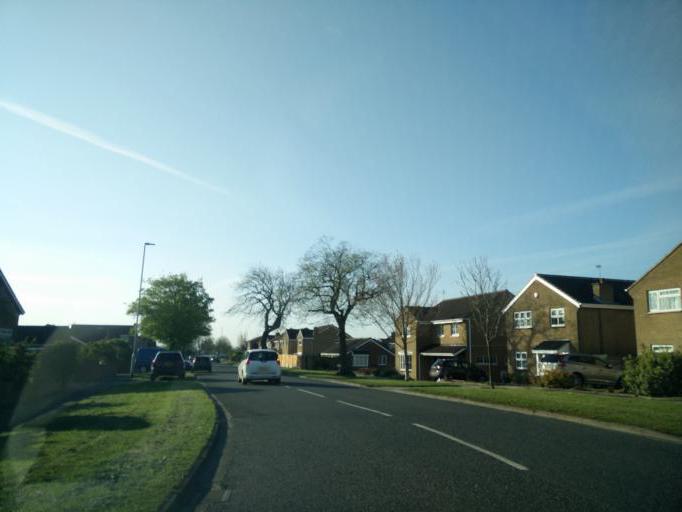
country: GB
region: England
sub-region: Stockton-on-Tees
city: Billingham
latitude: 54.6152
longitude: -1.3169
